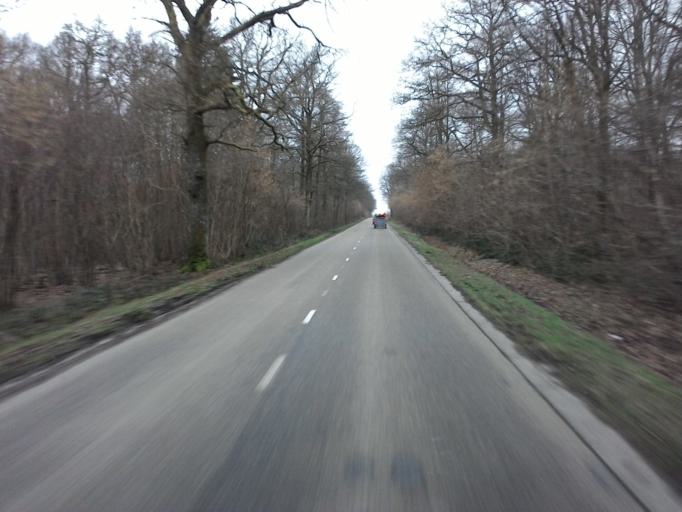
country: BE
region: Wallonia
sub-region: Province de Namur
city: Beauraing
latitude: 50.0473
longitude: 4.9700
